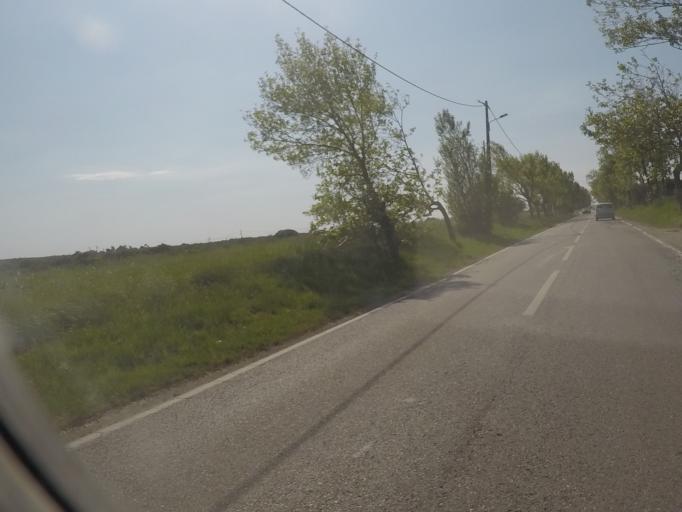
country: PT
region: Setubal
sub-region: Sesimbra
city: Sesimbra
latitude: 38.4440
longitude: -9.1468
